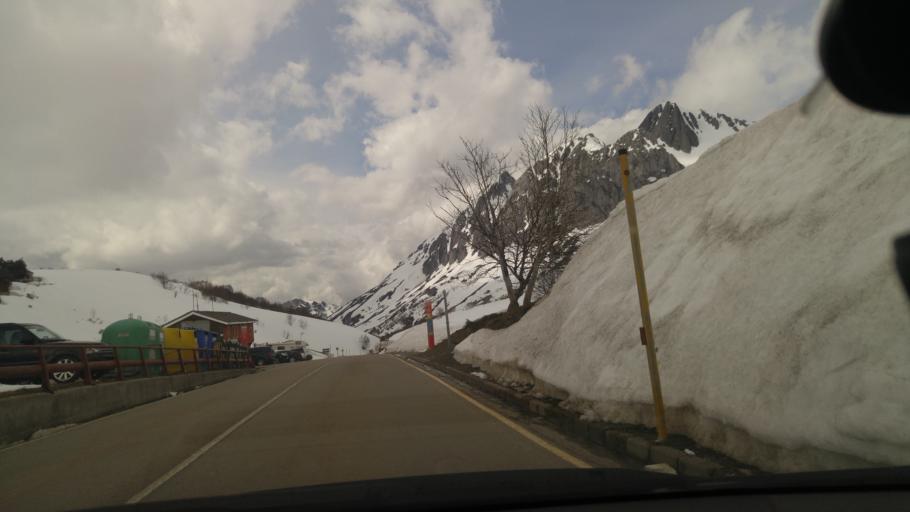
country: ES
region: Asturias
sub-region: Province of Asturias
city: Campo de Caso
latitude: 43.0656
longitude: -5.3872
